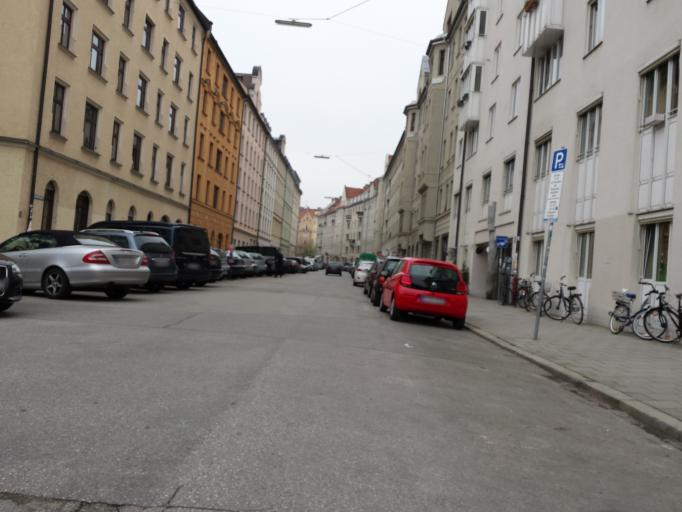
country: DE
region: Bavaria
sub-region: Upper Bavaria
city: Munich
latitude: 48.1226
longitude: 11.5626
